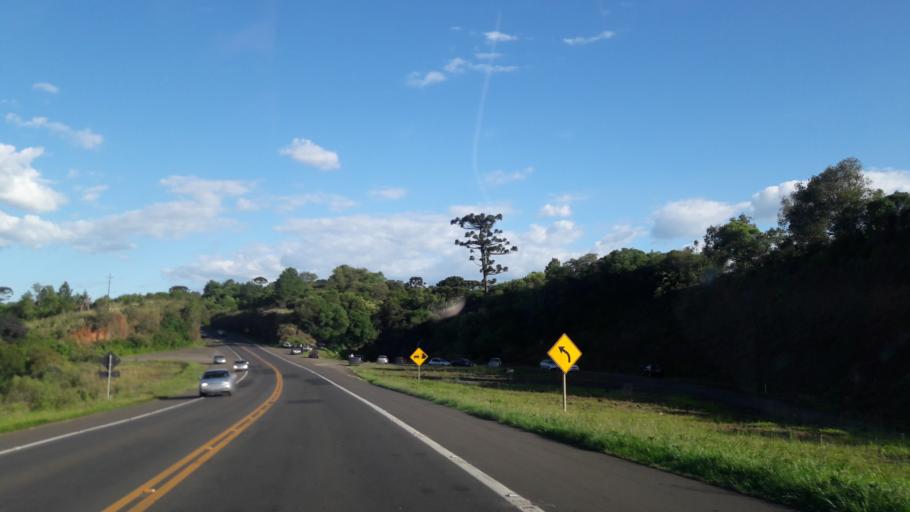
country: BR
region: Parana
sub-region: Guarapuava
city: Guarapuava
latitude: -25.3572
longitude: -51.3595
